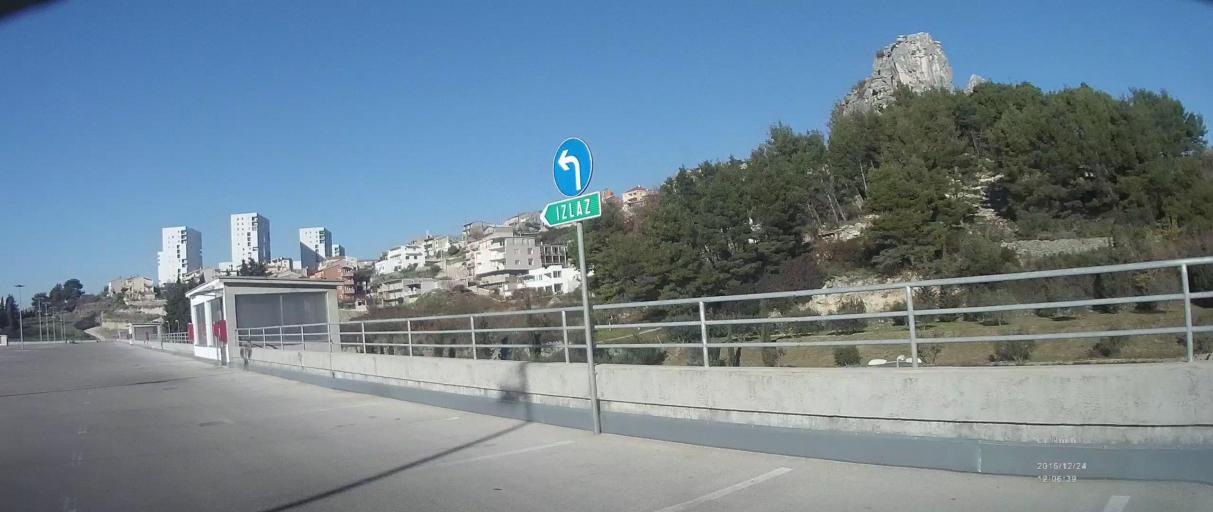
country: HR
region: Splitsko-Dalmatinska
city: Kamen
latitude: 43.5142
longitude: 16.5044
